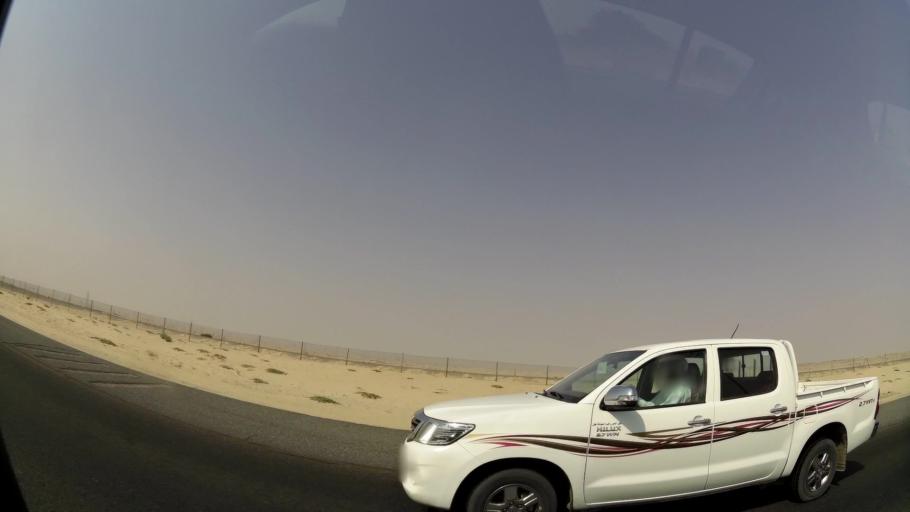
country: KW
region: Muhafazat al Jahra'
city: Al Jahra'
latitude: 29.3533
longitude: 47.6324
